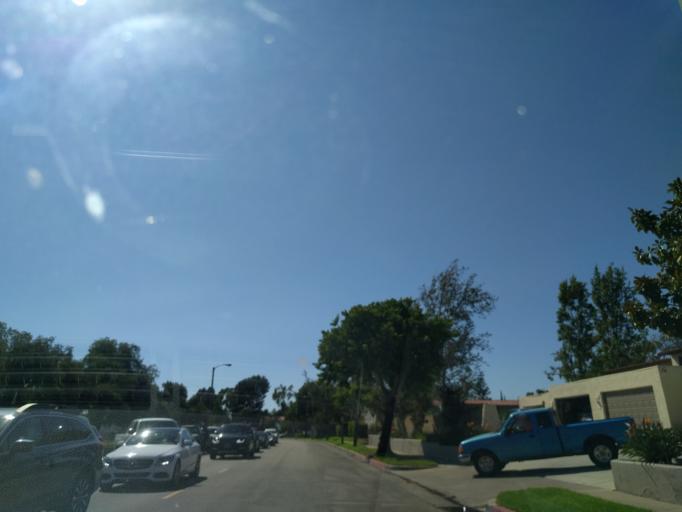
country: US
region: California
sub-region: Orange County
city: Costa Mesa
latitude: 33.6362
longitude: -117.8775
